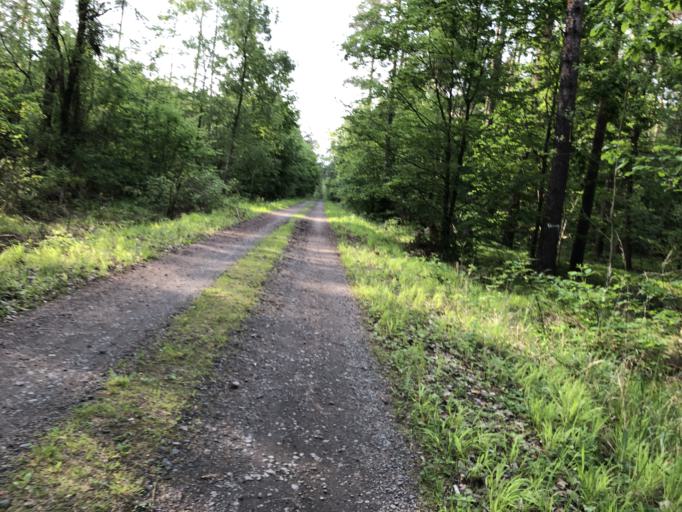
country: DE
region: Bavaria
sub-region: Upper Franconia
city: Memmelsdorf
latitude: 49.9075
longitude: 10.9575
